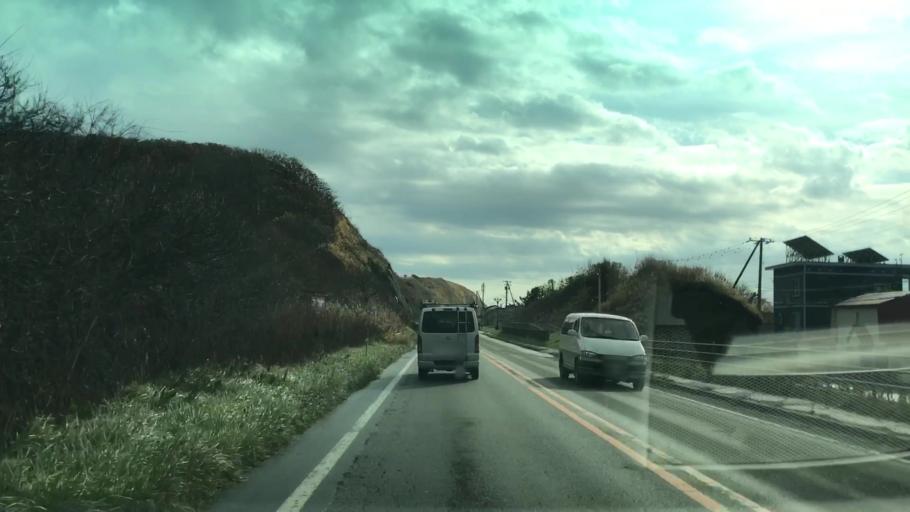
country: JP
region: Hokkaido
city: Shizunai-furukawacho
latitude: 42.1501
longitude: 142.8037
